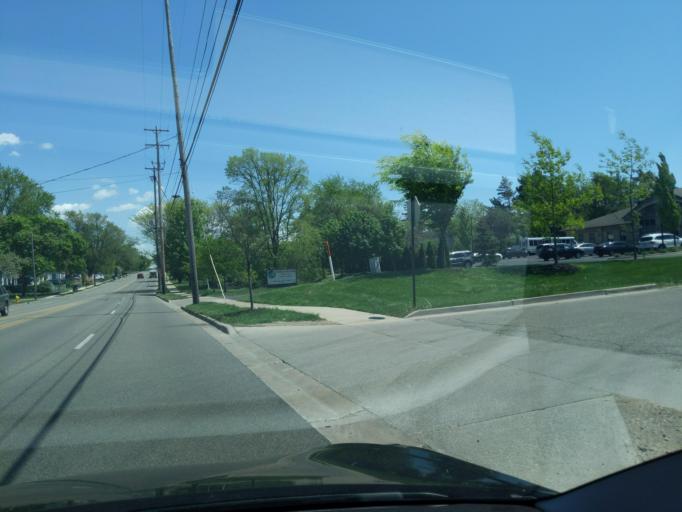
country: US
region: Michigan
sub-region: Kent County
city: East Grand Rapids
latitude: 42.9271
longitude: -85.6046
